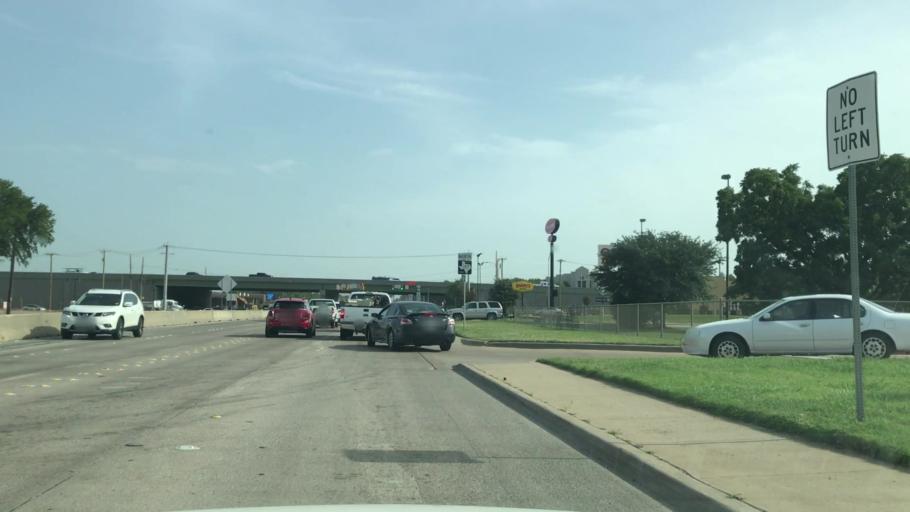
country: US
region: Texas
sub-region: Tarrant County
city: Euless
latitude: 32.8354
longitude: -97.0997
